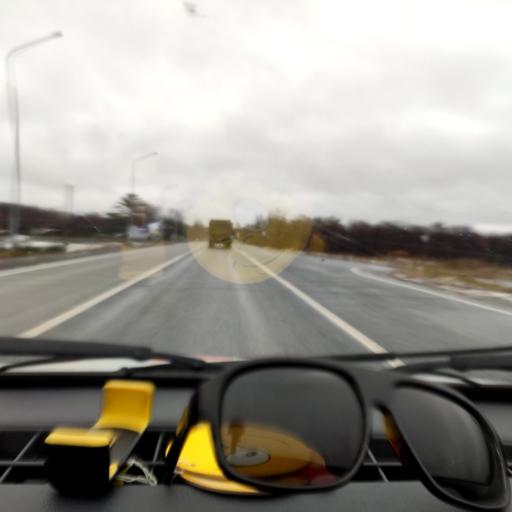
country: RU
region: Bashkortostan
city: Urman
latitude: 54.8238
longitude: 56.8887
